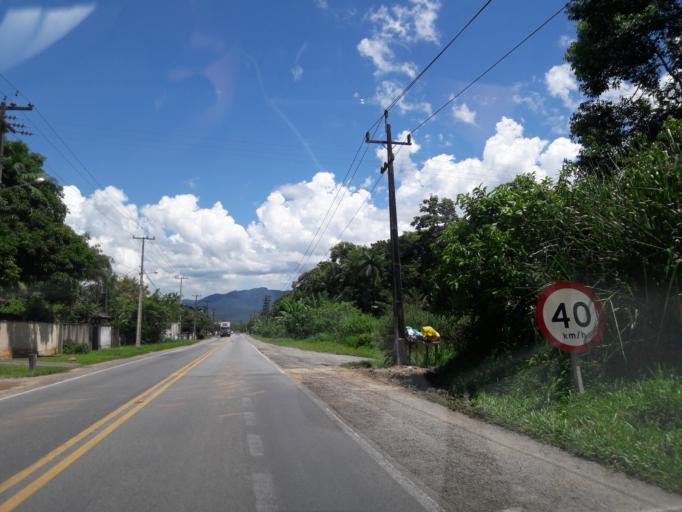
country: BR
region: Parana
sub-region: Antonina
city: Antonina
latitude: -25.4656
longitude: -48.8257
